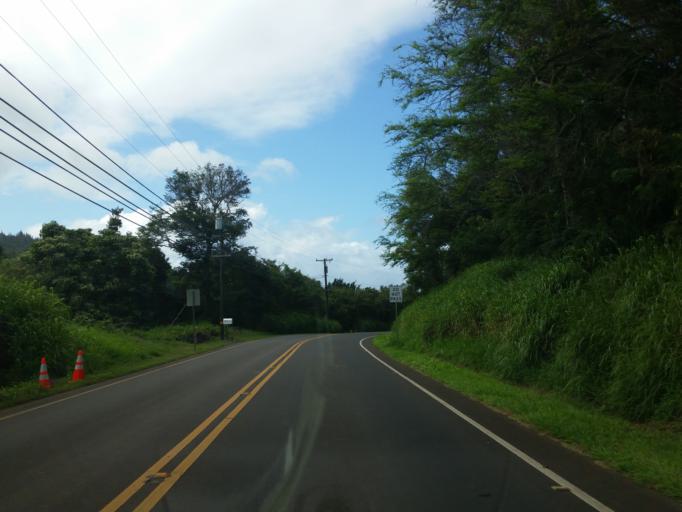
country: US
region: Hawaii
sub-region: Maui County
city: Waihee-Waiehu
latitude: 20.9393
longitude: -156.5142
